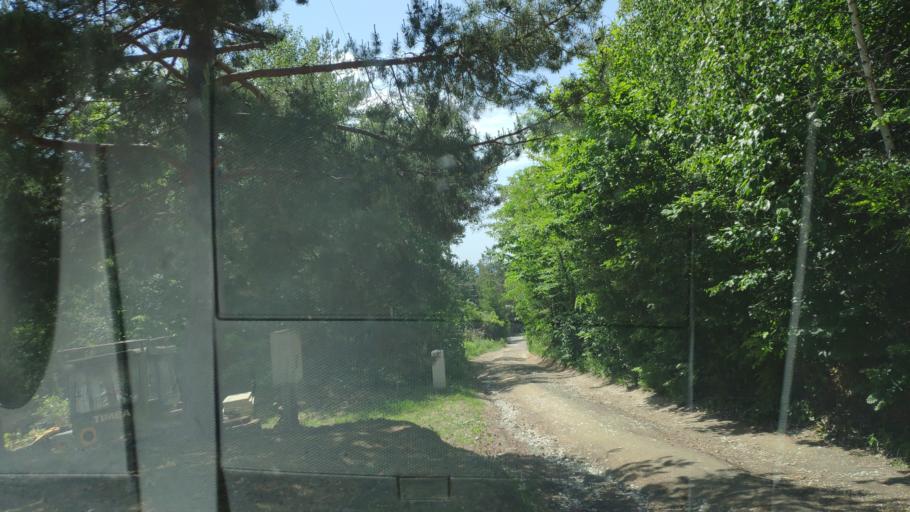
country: SK
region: Kosicky
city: Medzev
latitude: 48.7175
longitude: 20.9808
